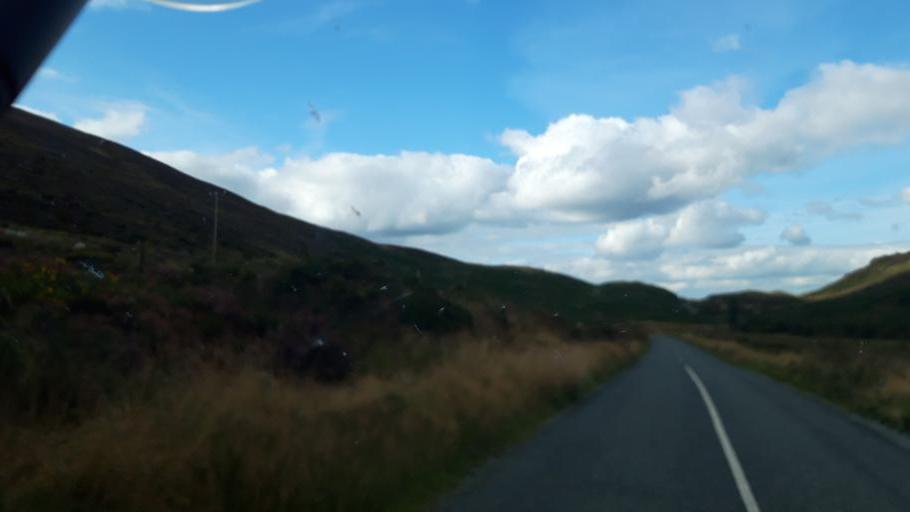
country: GB
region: Northern Ireland
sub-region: Down District
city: Warrenpoint
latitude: 54.0535
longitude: -6.2717
